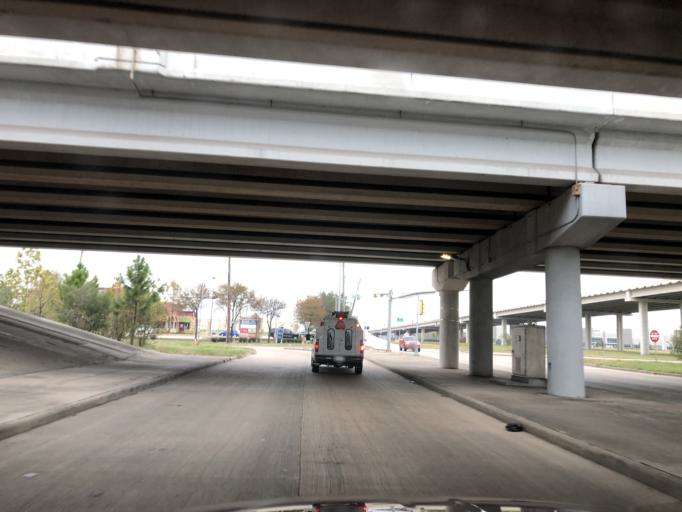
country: US
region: Texas
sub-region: Fort Bend County
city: Missouri City
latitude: 29.6138
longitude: -95.4949
